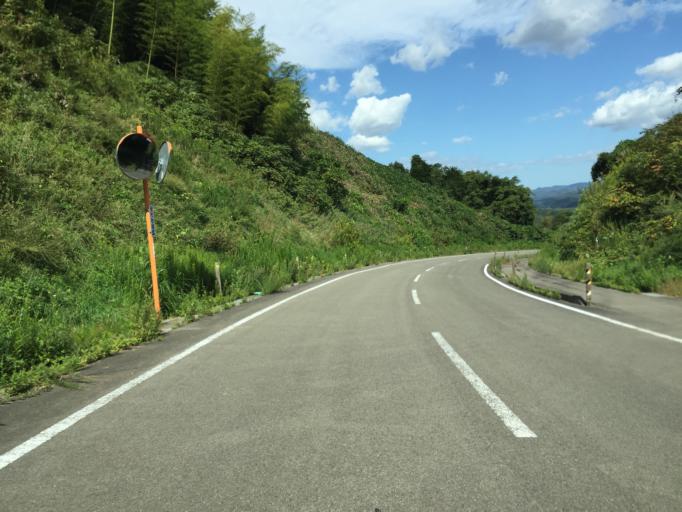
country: JP
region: Fukushima
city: Hobaramachi
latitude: 37.7779
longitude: 140.5380
